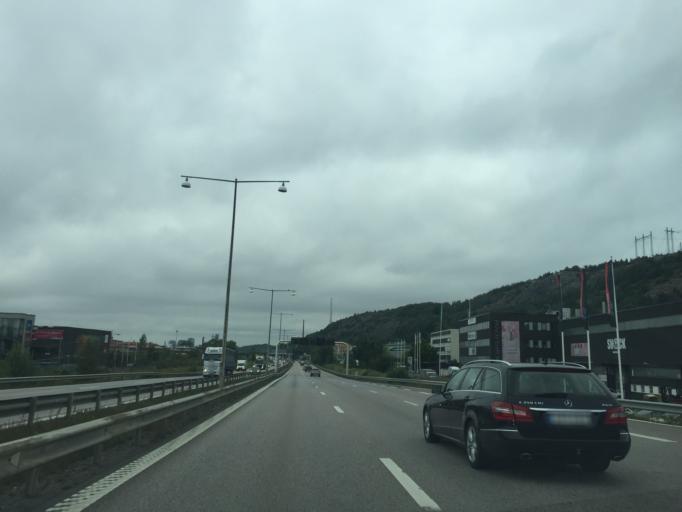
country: SE
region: Vaestra Goetaland
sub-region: Molndal
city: Moelndal
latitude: 57.6680
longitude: 12.0144
